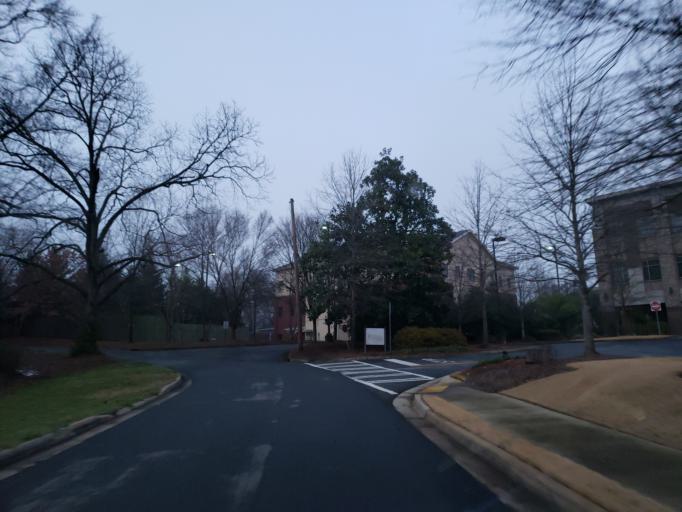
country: US
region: Georgia
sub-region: Cobb County
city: Marietta
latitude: 33.9730
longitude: -84.5543
